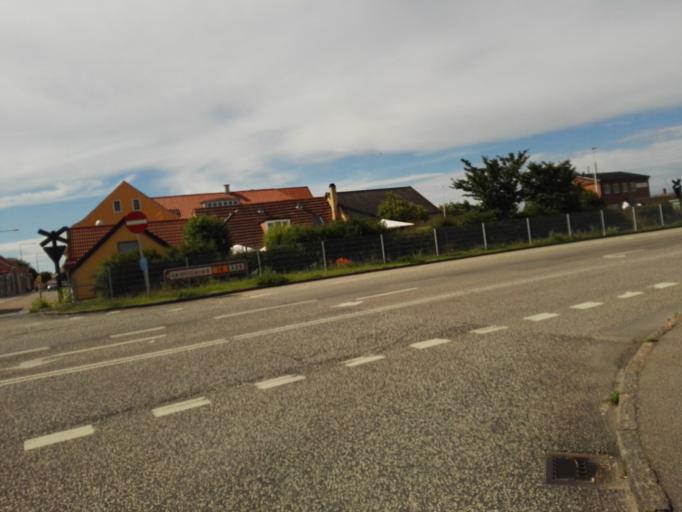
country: DK
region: Capital Region
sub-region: Halsnaes Kommune
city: Hundested
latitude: 55.9665
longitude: 11.8494
